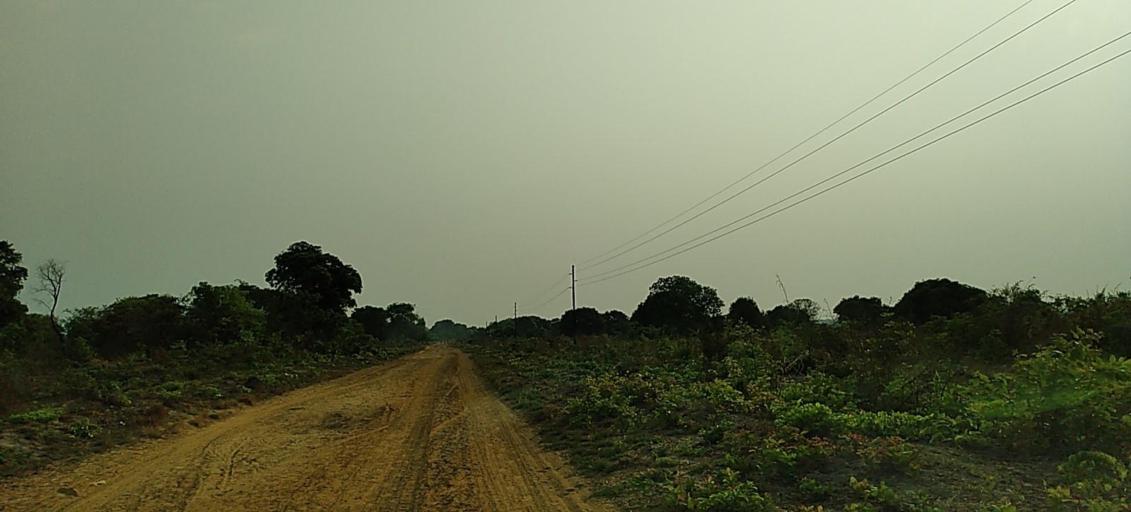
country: ZM
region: North-Western
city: Zambezi
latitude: -13.4773
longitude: 23.1272
